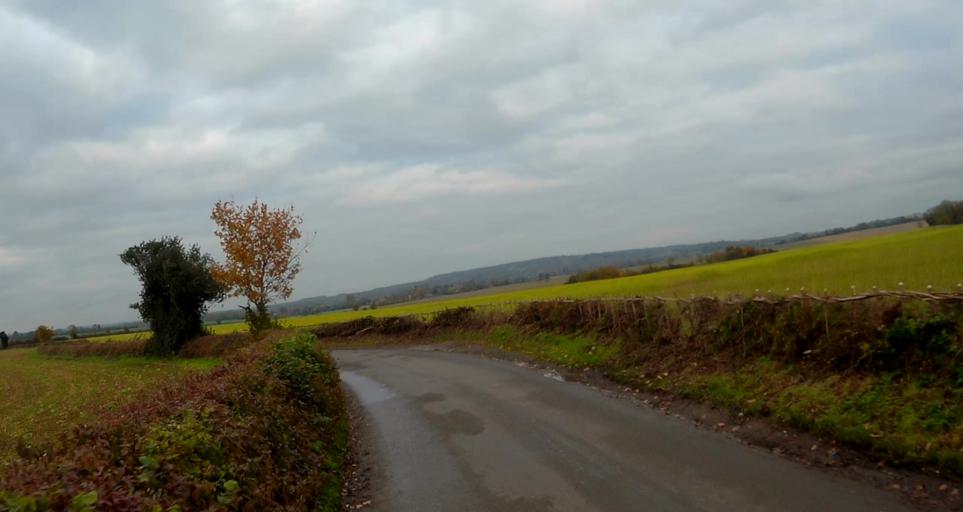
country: GB
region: England
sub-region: Hampshire
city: Long Sutton
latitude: 51.2220
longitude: -0.8807
